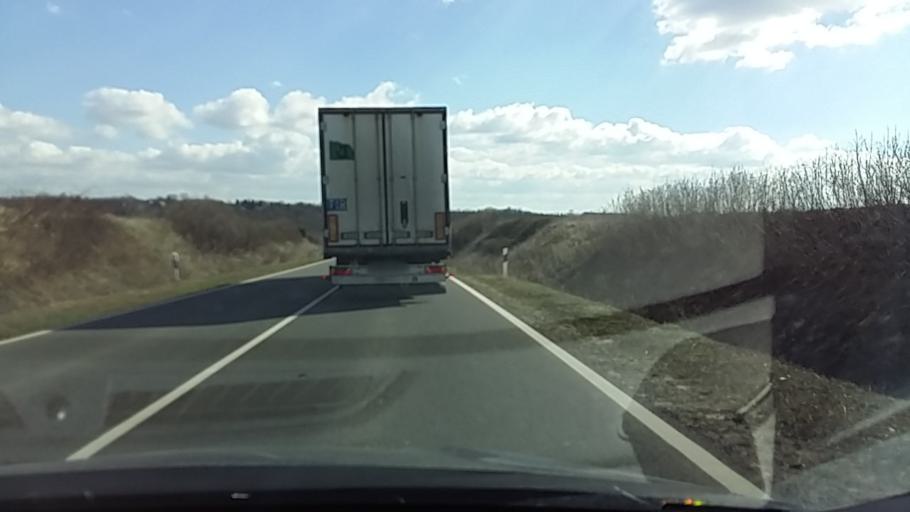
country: HU
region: Baranya
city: Kozarmisleny
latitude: 46.0313
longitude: 18.2746
